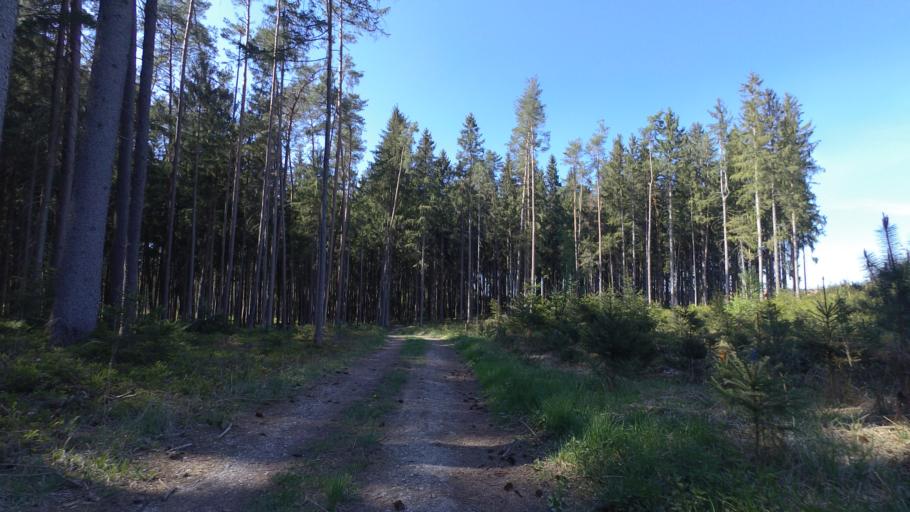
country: DE
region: Bavaria
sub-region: Upper Bavaria
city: Traunreut
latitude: 47.9502
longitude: 12.5388
